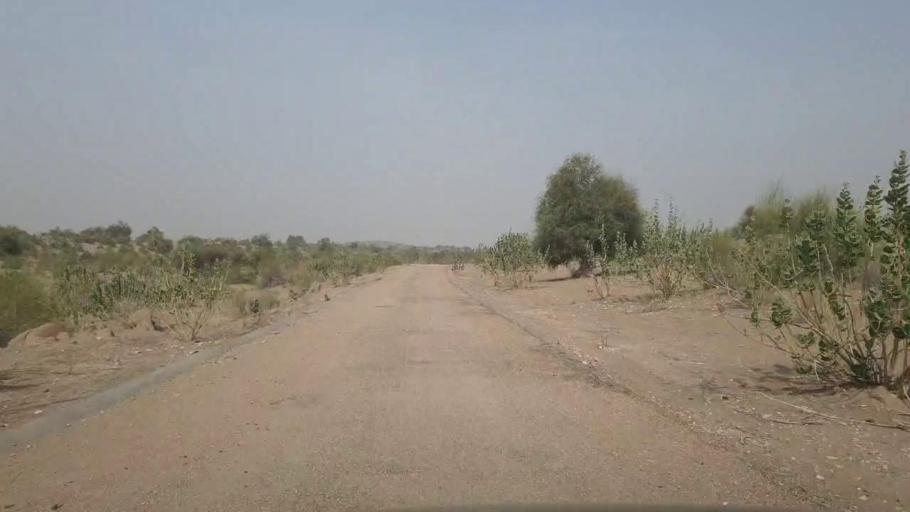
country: PK
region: Sindh
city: Chor
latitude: 25.6041
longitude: 69.9906
